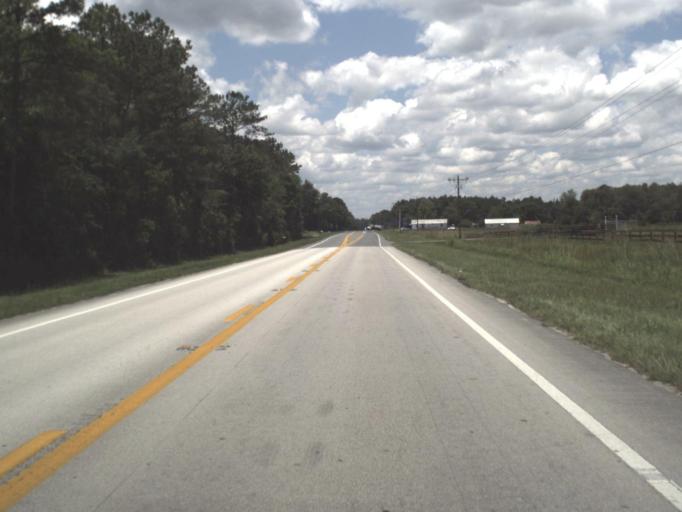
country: US
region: Florida
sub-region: Alachua County
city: Waldo
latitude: 29.7138
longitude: -82.1028
